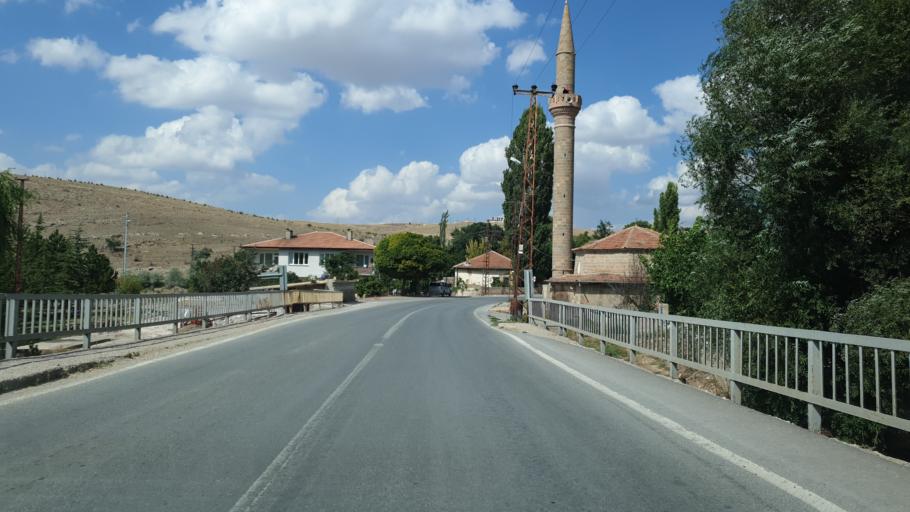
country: TR
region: Kayseri
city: Felahiye
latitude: 39.0927
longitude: 35.5696
